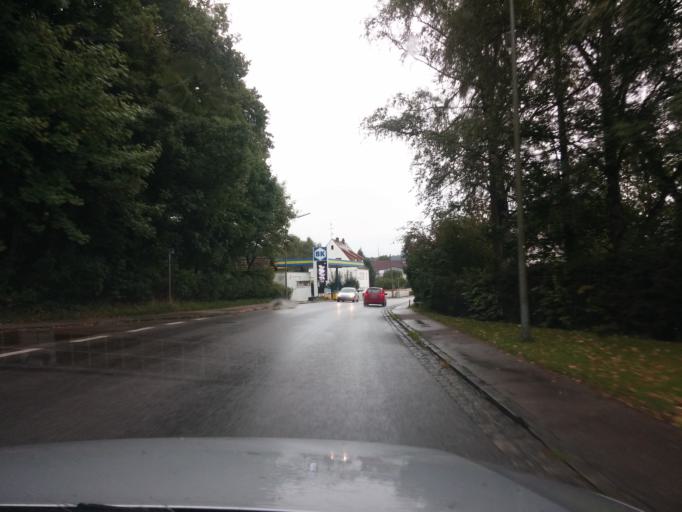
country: DE
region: Bavaria
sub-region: Upper Bavaria
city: Reichertshausen
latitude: 48.4698
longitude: 11.5091
